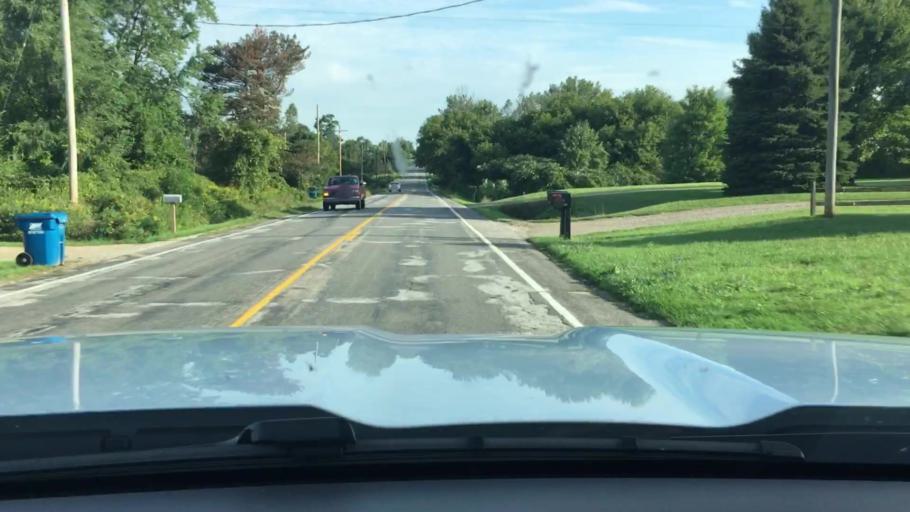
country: US
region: Michigan
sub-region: Kent County
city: Kent City
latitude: 43.2054
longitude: -85.7709
